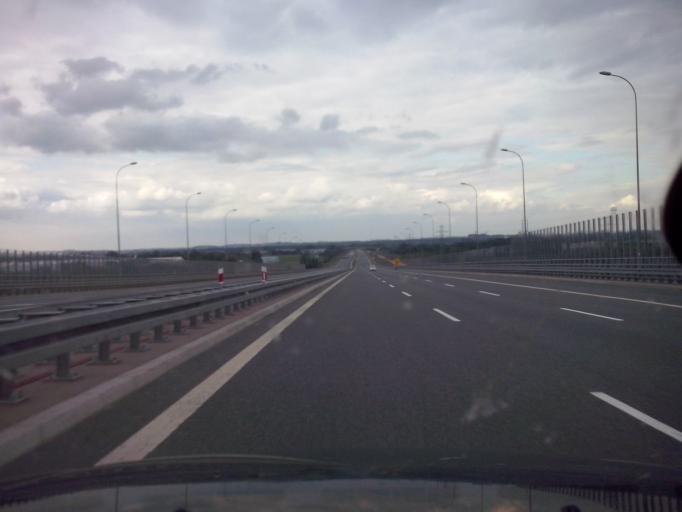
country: PL
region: Lesser Poland Voivodeship
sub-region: Powiat wielicki
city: Czarnochowice
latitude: 50.0173
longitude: 20.0618
